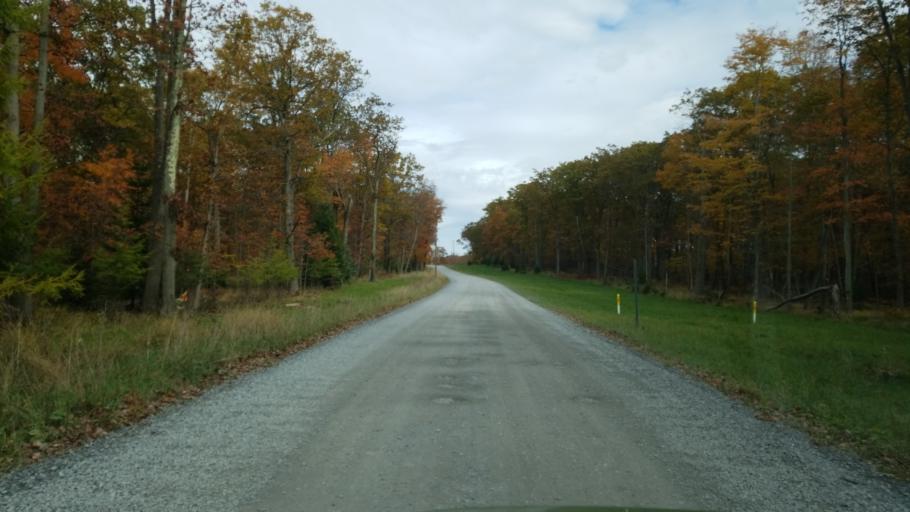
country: US
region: Pennsylvania
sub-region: Clearfield County
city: Clearfield
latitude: 41.1568
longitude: -78.4585
